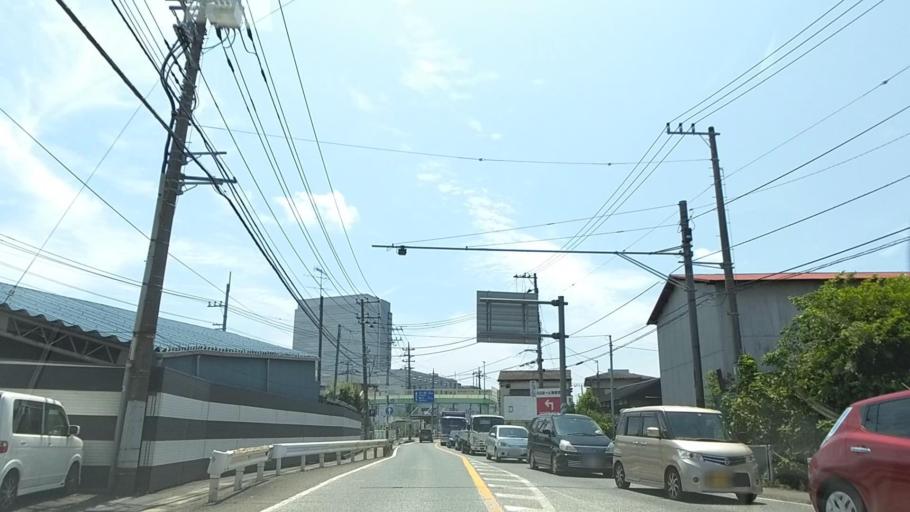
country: JP
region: Kanagawa
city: Zama
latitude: 35.4635
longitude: 139.3886
